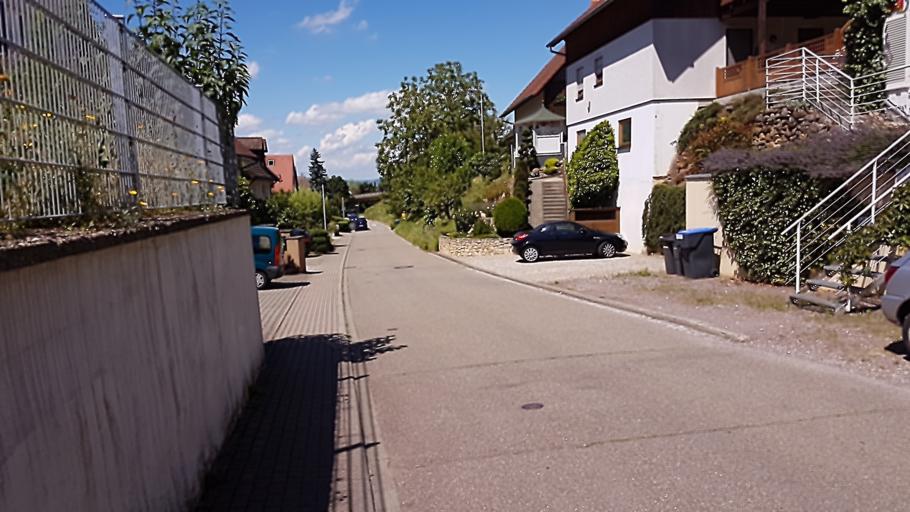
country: DE
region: Baden-Wuerttemberg
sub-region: Freiburg Region
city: Ebringen
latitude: 47.9520
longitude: 7.7754
